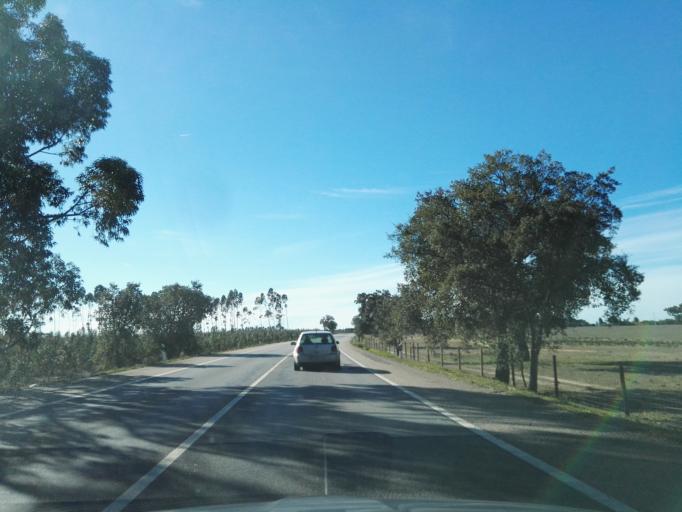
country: PT
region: Portalegre
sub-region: Gaviao
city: Gaviao
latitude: 39.4457
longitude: -7.7989
